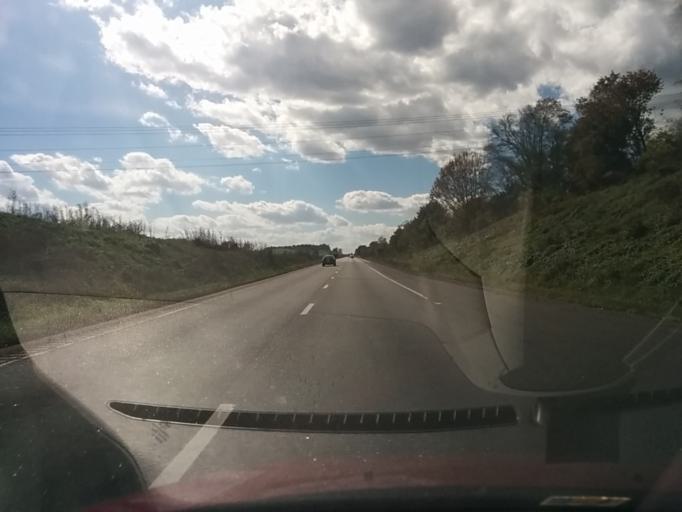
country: US
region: Virginia
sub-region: Rockbridge County
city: East Lexington
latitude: 37.8828
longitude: -79.2925
